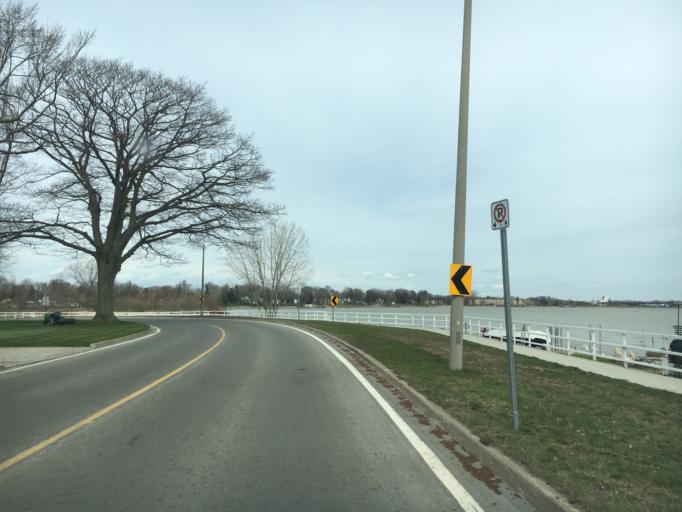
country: CA
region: Ontario
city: Port Colborne
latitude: 42.8744
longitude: -79.2720
